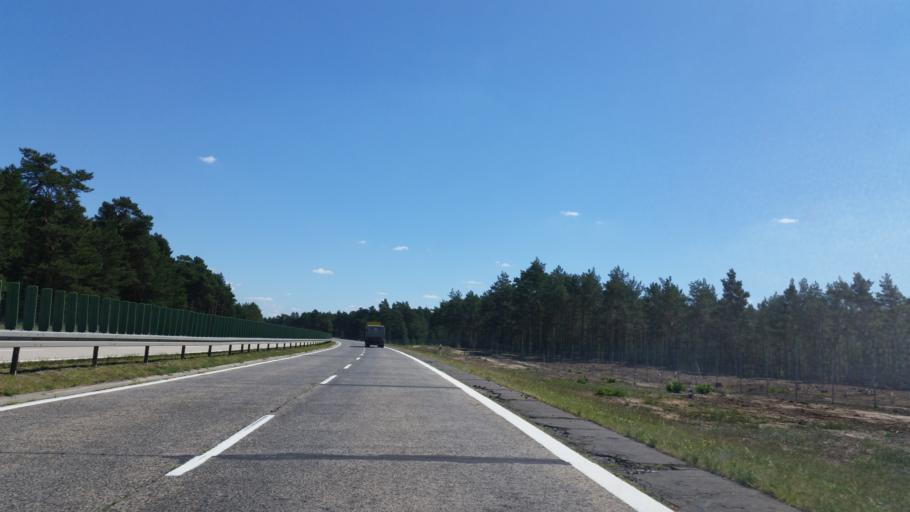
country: PL
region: Lubusz
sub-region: Powiat zaganski
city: Malomice
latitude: 51.4331
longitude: 15.3730
